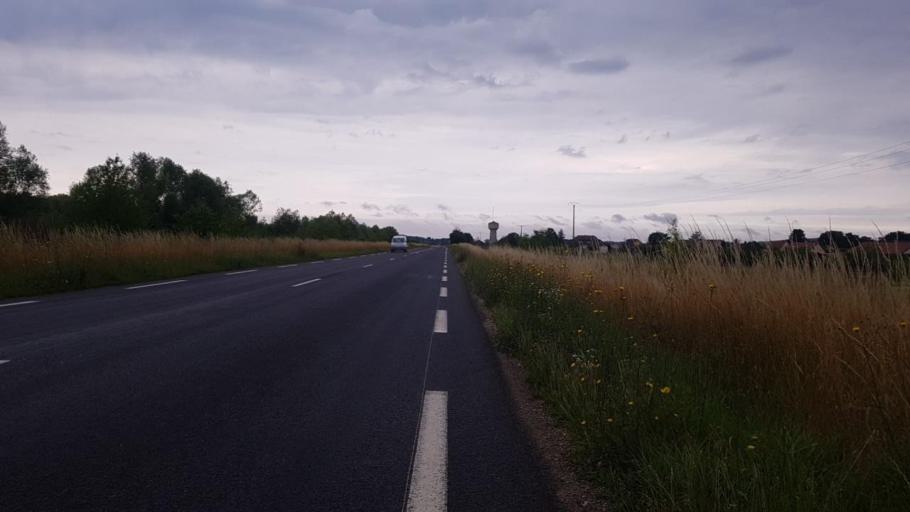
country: FR
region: Champagne-Ardenne
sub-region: Departement de la Marne
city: Vitry-le-Francois
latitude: 48.7446
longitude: 4.6807
